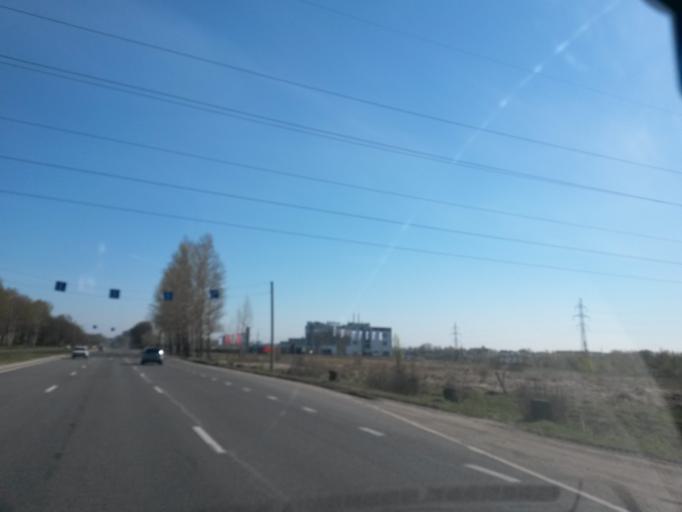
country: RU
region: Jaroslavl
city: Krasnyye Tkachi
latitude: 57.5561
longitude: 39.8172
